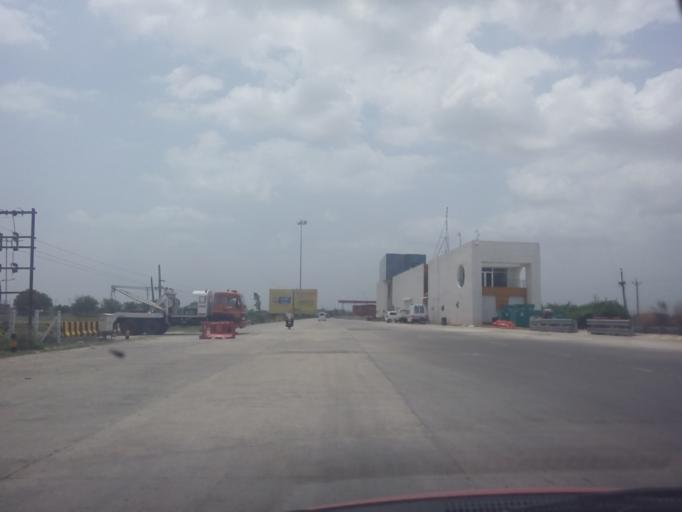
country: IN
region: Gujarat
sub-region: Ahmadabad
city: Sanand
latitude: 23.0080
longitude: 72.3470
